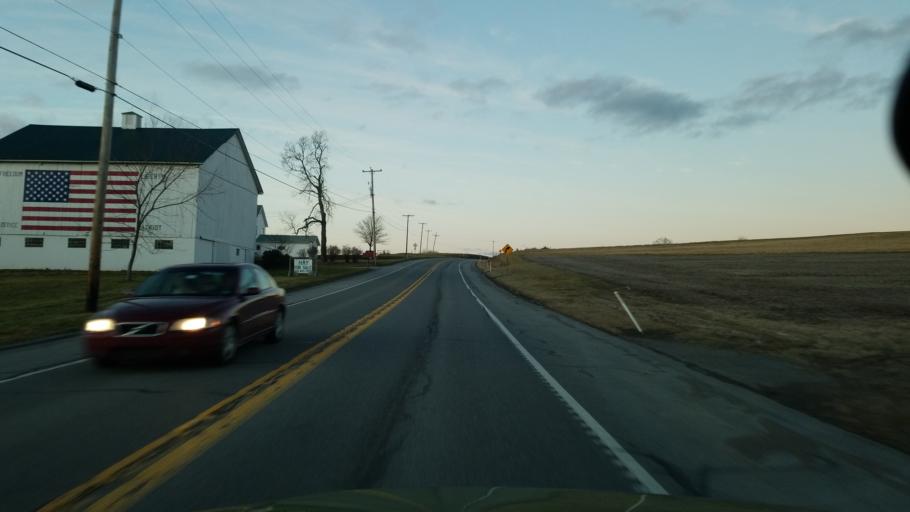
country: US
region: Pennsylvania
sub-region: Jefferson County
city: Punxsutawney
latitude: 40.8946
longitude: -79.0170
